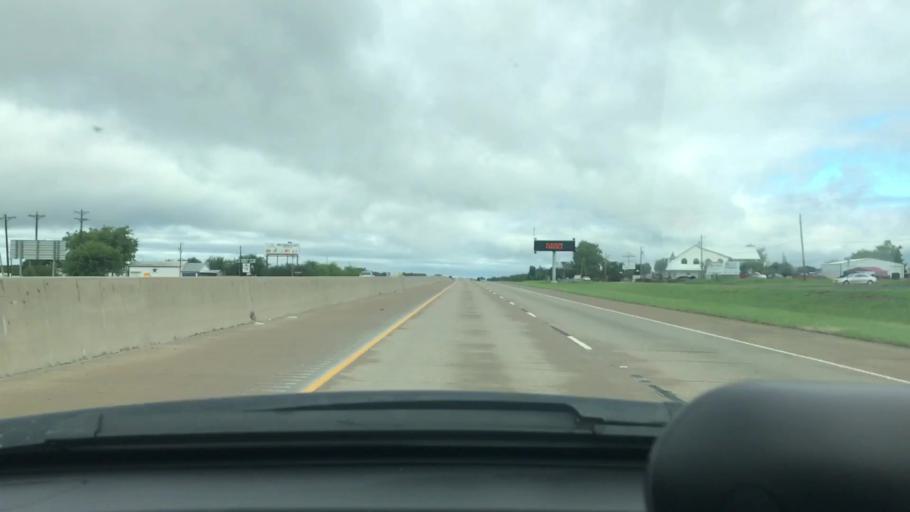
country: US
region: Texas
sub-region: Grayson County
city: Van Alstyne
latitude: 33.4500
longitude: -96.6046
